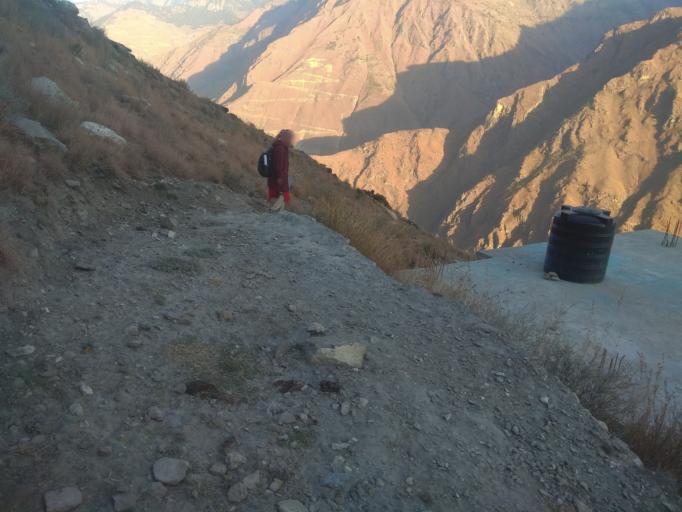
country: NP
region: Mid Western
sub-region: Bheri Zone
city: Dailekh
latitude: 29.2632
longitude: 81.6878
